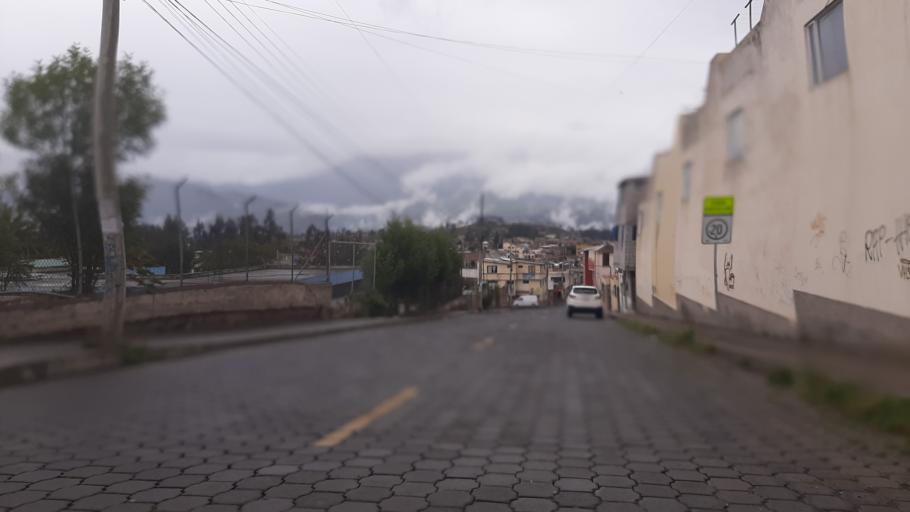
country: EC
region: Chimborazo
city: Riobamba
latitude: -1.6551
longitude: -78.6428
